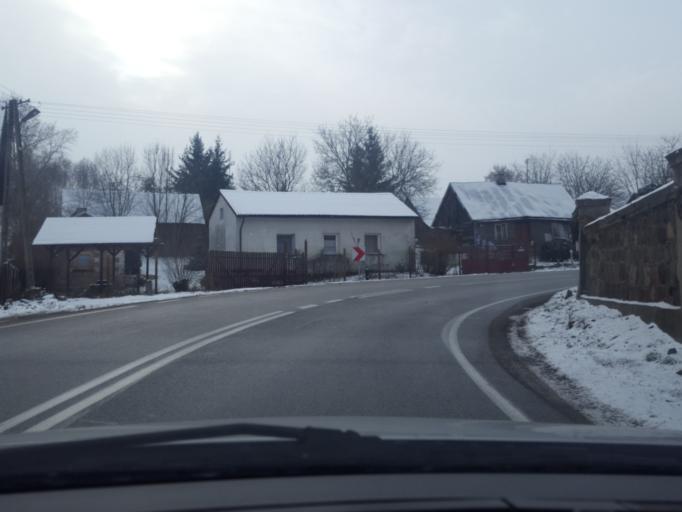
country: PL
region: Lodz Voivodeship
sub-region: Powiat brzezinski
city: Rogow
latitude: 51.8657
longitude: 19.8311
